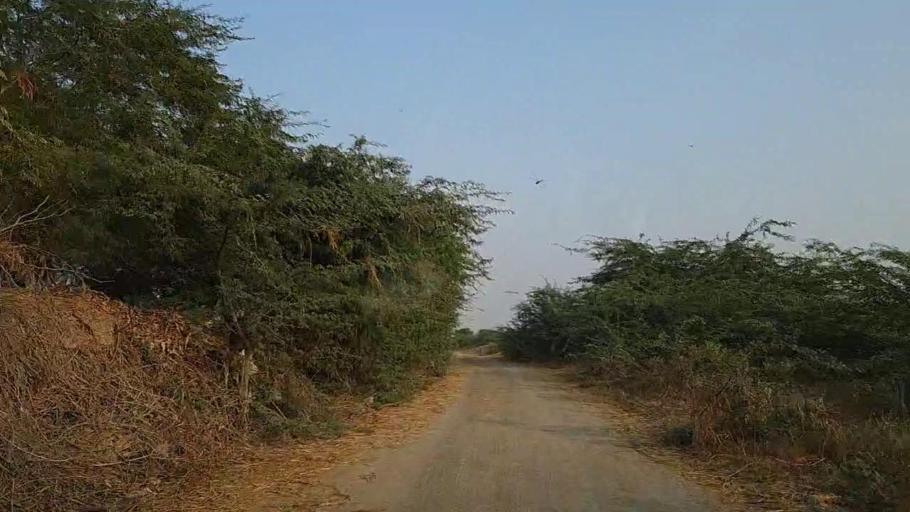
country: PK
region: Sindh
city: Thatta
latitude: 24.6895
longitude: 67.8184
